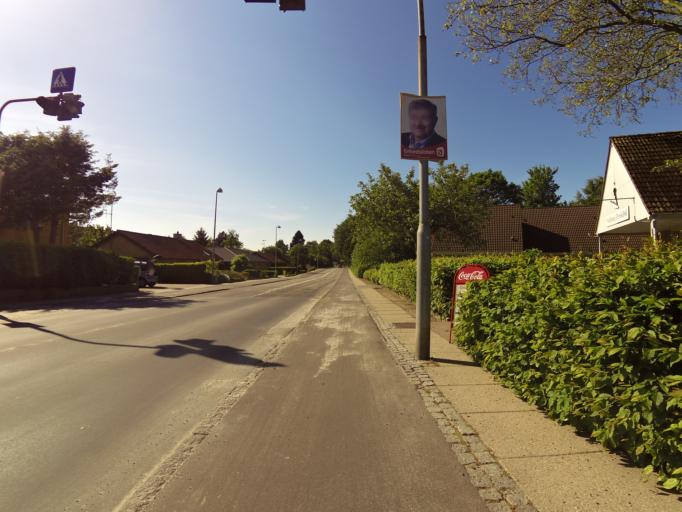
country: DK
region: Capital Region
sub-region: Gladsaxe Municipality
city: Buddinge
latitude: 55.7694
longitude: 12.4798
